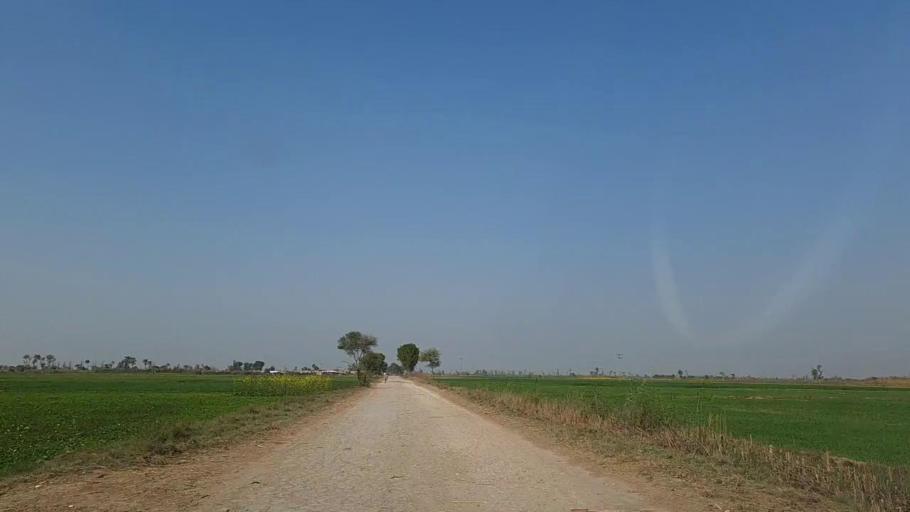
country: PK
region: Sindh
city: Daur
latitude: 26.4724
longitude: 68.2970
